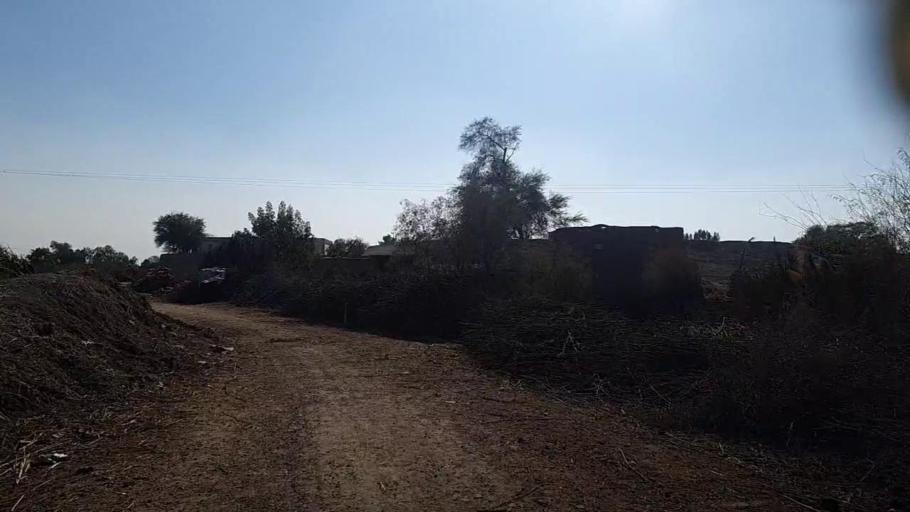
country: PK
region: Sindh
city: Khairpur
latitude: 27.9493
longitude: 69.7505
